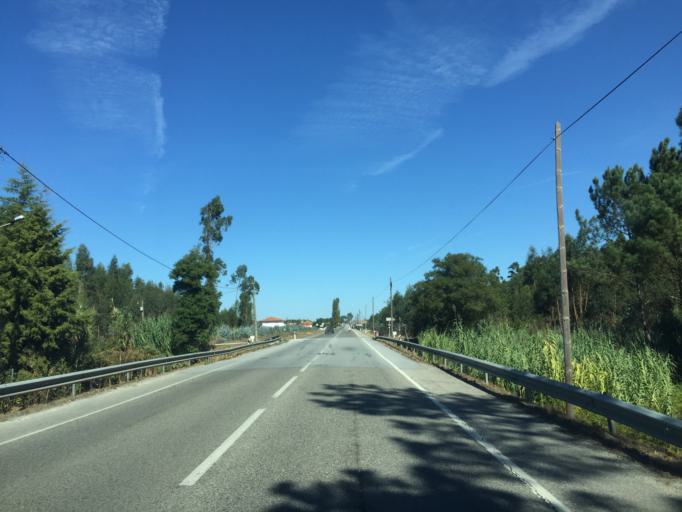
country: PT
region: Coimbra
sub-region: Figueira da Foz
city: Alhadas
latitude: 40.2468
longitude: -8.7876
